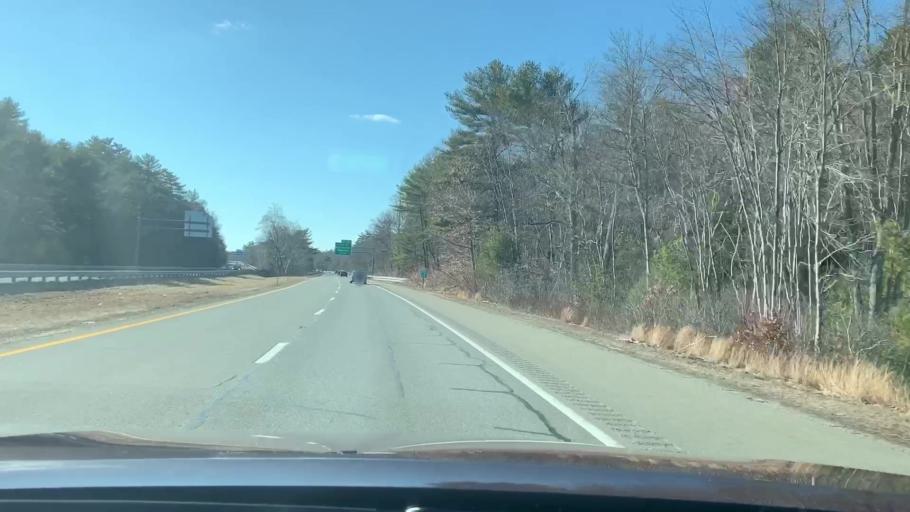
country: US
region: Massachusetts
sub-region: Essex County
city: Essex
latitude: 42.5915
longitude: -70.7762
